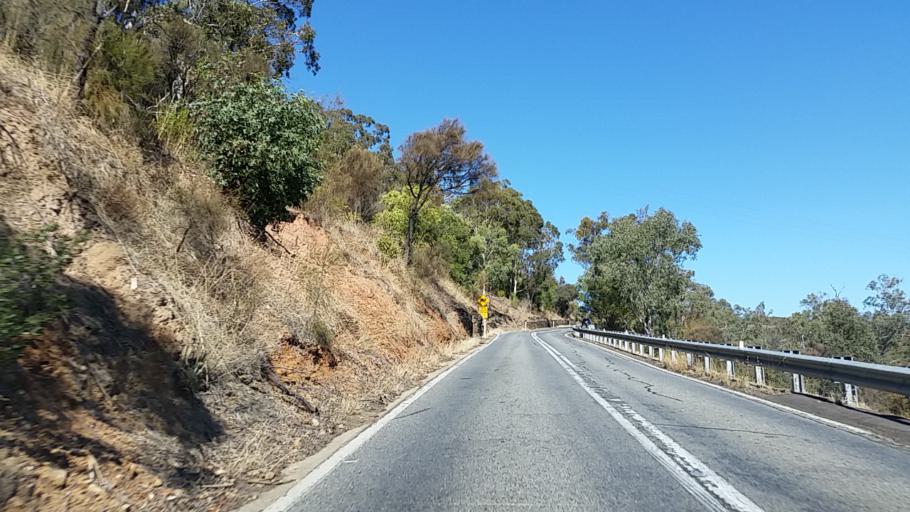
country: AU
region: South Australia
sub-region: Burnside
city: Beaumont
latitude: -34.9492
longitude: 138.6802
